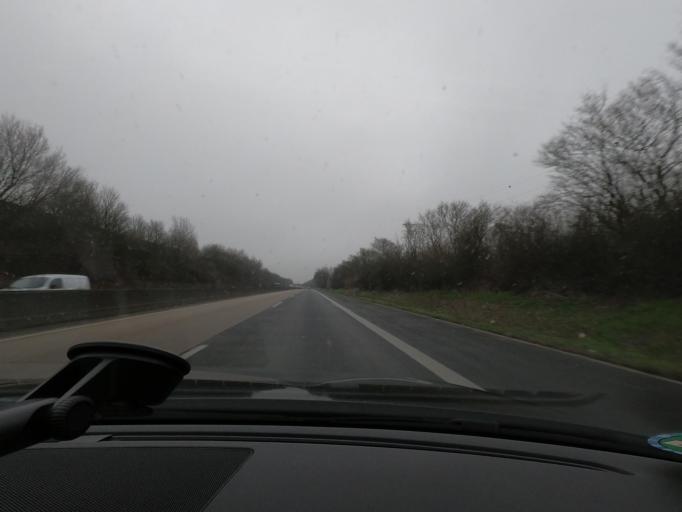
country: DE
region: North Rhine-Westphalia
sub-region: Regierungsbezirk Koln
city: Bedburg
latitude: 50.9777
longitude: 6.5591
